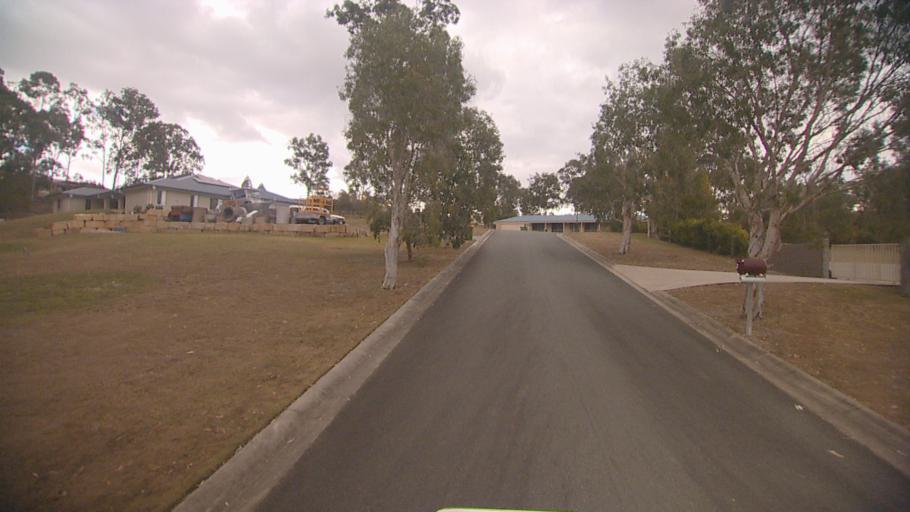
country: AU
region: Queensland
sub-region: Logan
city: Cedar Vale
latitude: -27.8735
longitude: 153.0768
